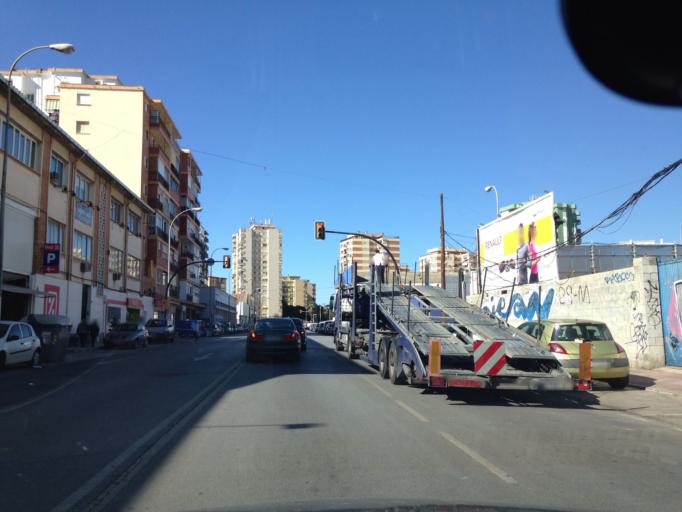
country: ES
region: Andalusia
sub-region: Provincia de Malaga
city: Malaga
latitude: 36.6924
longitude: -4.4513
